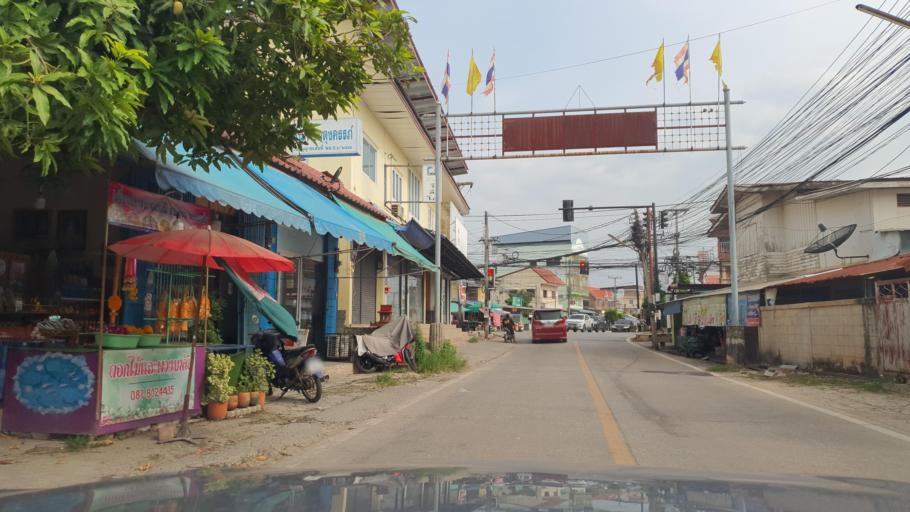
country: TH
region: Phitsanulok
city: Phitsanulok
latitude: 16.8498
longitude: 100.2553
